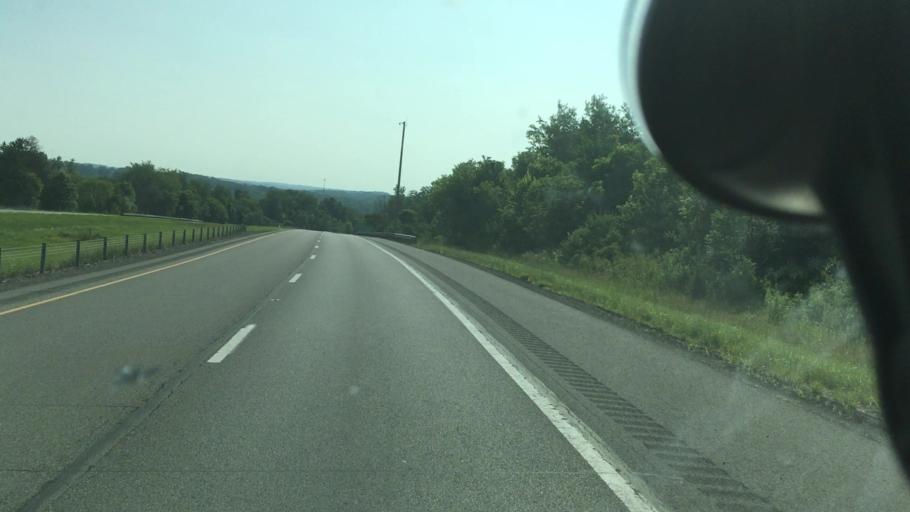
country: US
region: Pennsylvania
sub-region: Lawrence County
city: Oakland
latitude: 40.9686
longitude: -80.3479
